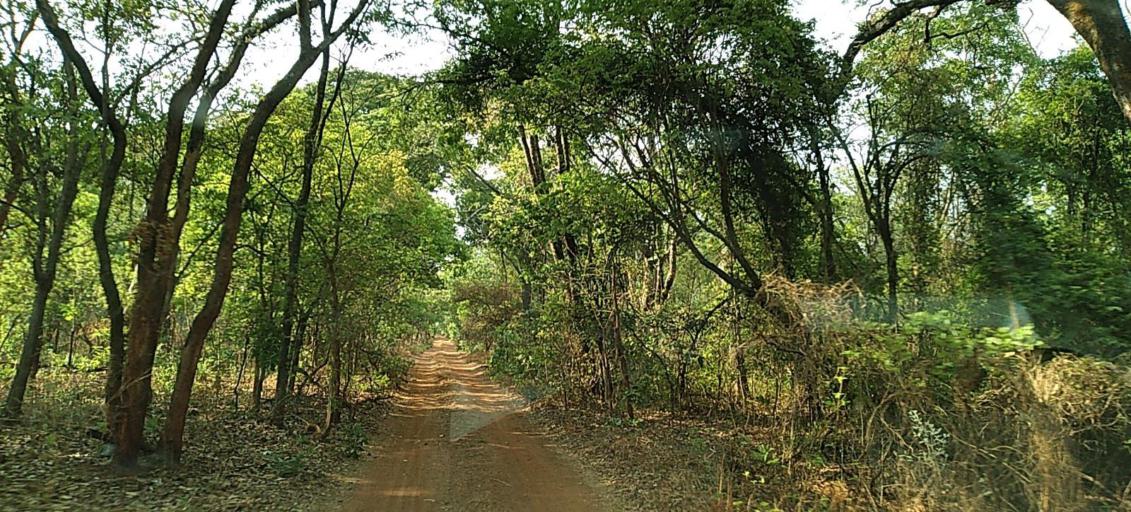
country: ZM
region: Copperbelt
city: Kalulushi
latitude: -12.9807
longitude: 27.7180
